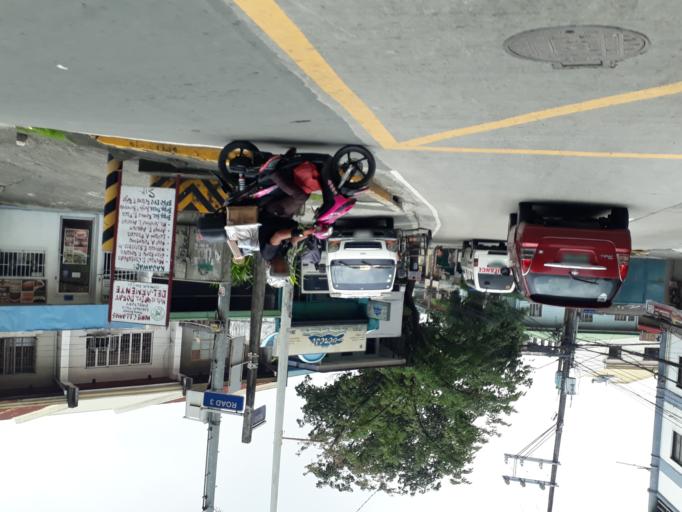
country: PH
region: Calabarzon
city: Bagong Pagasa
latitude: 14.6597
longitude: 121.0441
